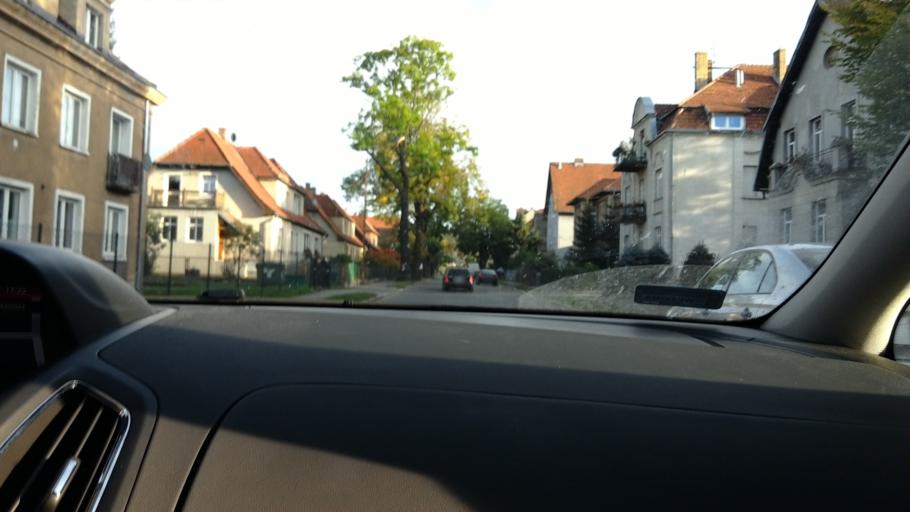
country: PL
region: Lower Silesian Voivodeship
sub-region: Jelenia Gora
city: Jelenia Gora
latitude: 50.8921
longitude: 15.7268
